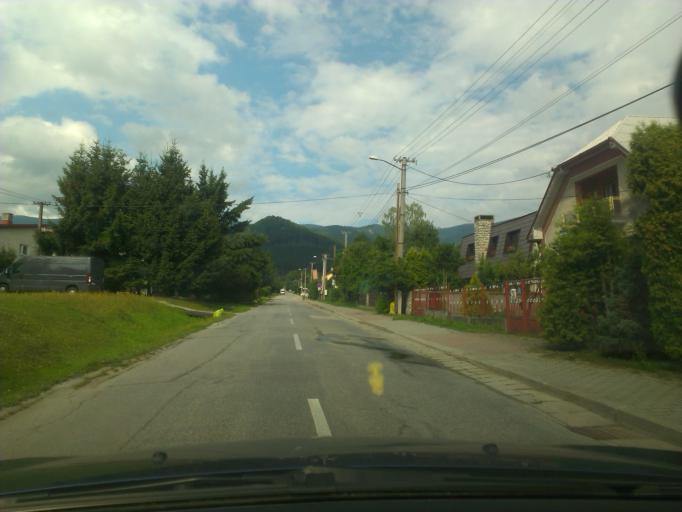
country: SK
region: Zilinsky
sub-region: Okres Zilina
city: Vrutky
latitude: 49.1080
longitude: 18.9084
